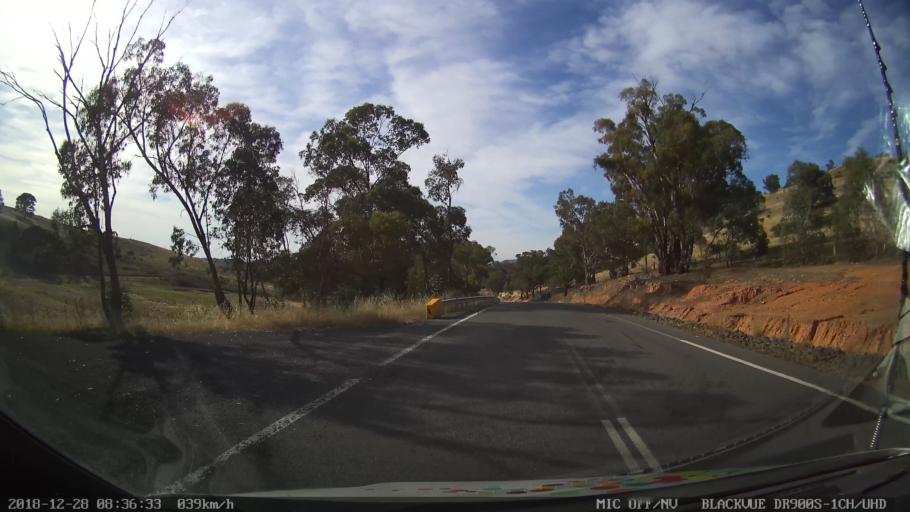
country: AU
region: New South Wales
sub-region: Blayney
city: Blayney
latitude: -33.9883
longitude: 149.3120
